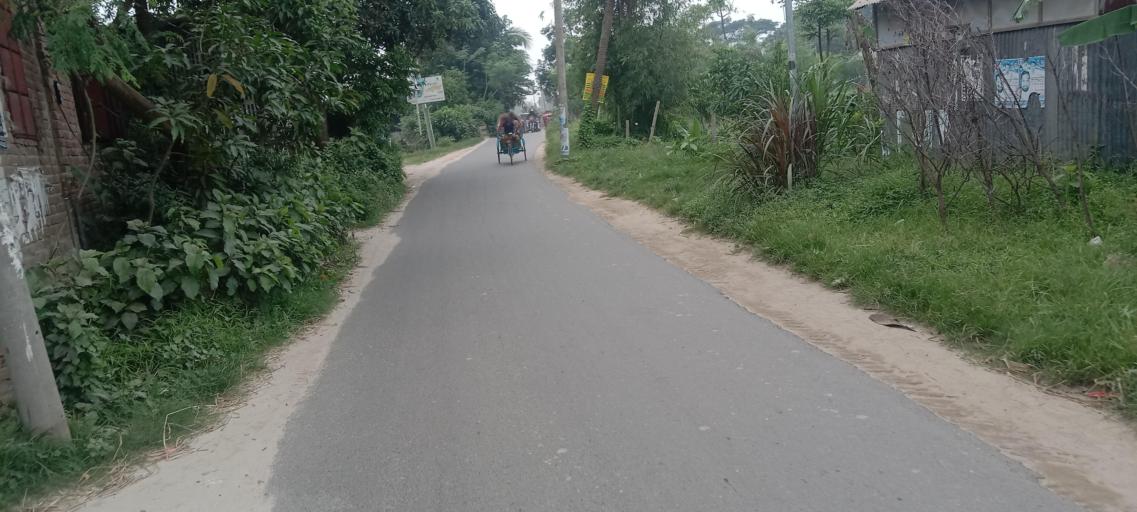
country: BD
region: Dhaka
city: Azimpur
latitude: 23.7362
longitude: 90.3202
